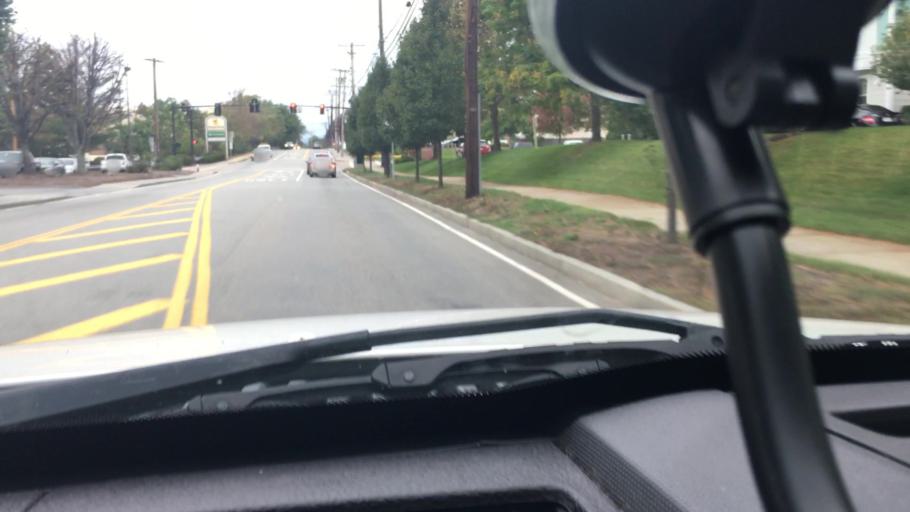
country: US
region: Massachusetts
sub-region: Middlesex County
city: Waltham
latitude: 42.3671
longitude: -71.2124
